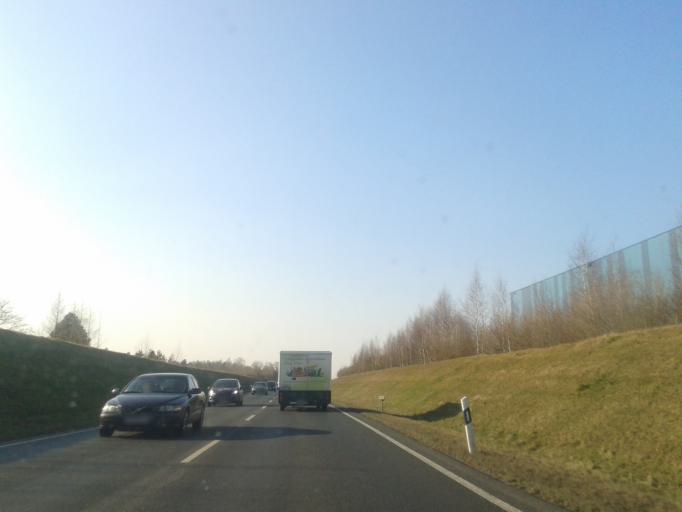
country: DE
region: Saxony
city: Nossen
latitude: 51.0261
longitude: 13.3001
